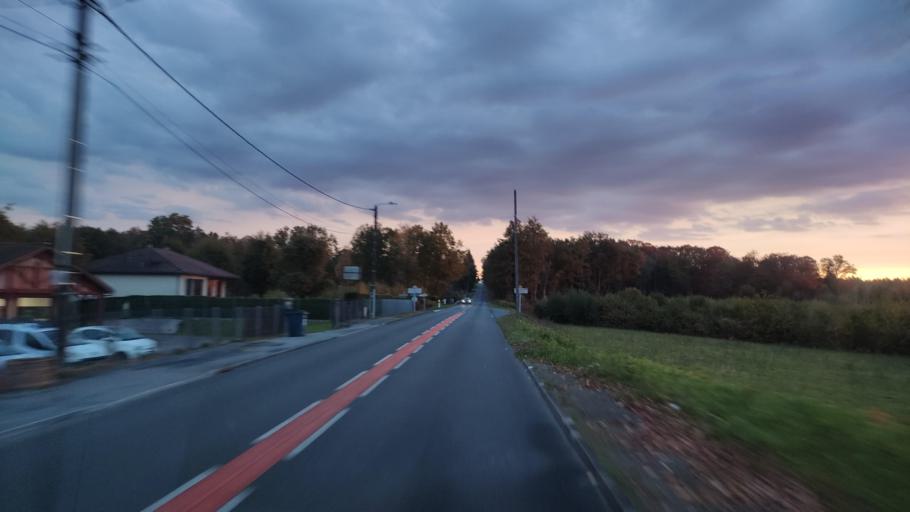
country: FR
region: Limousin
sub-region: Departement de la Haute-Vienne
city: Rilhac-Rancon
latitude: 45.9303
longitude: 1.3462
